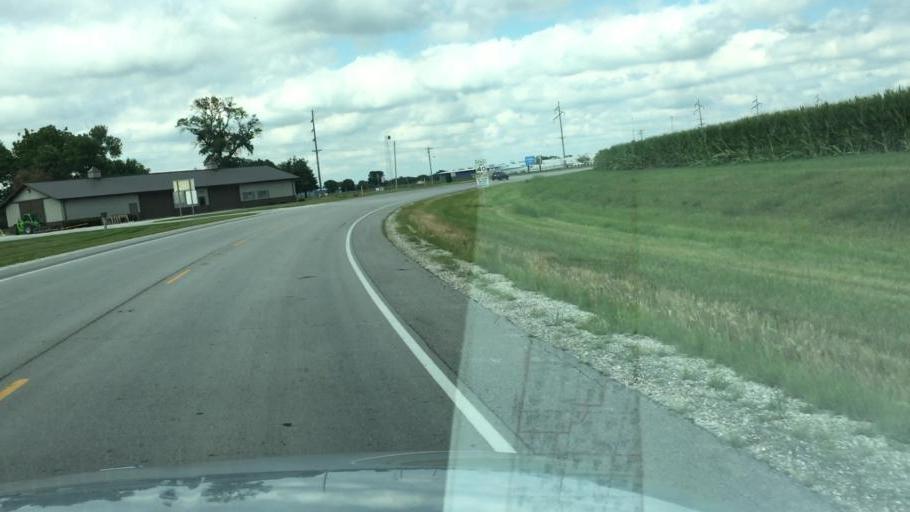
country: US
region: Illinois
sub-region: Hancock County
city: Carthage
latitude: 40.4154
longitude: -91.1543
